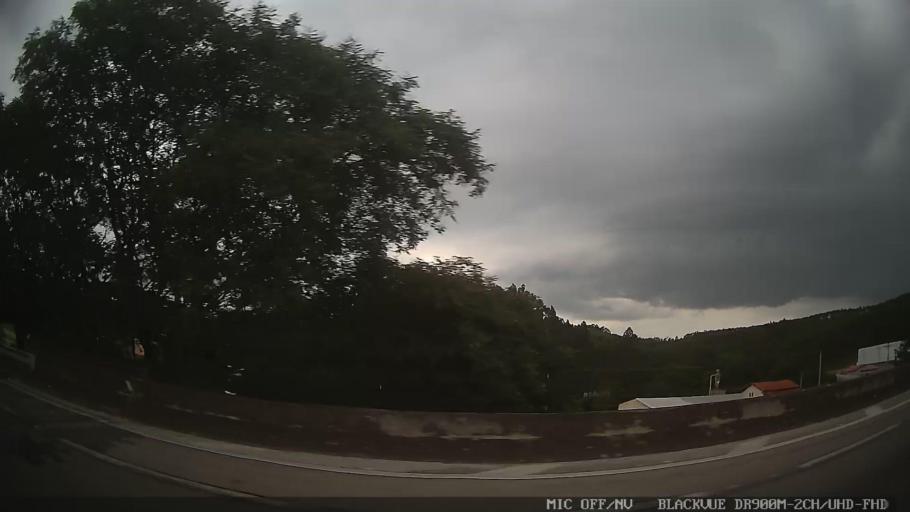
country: BR
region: Sao Paulo
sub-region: Jarinu
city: Jarinu
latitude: -23.0308
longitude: -46.7272
